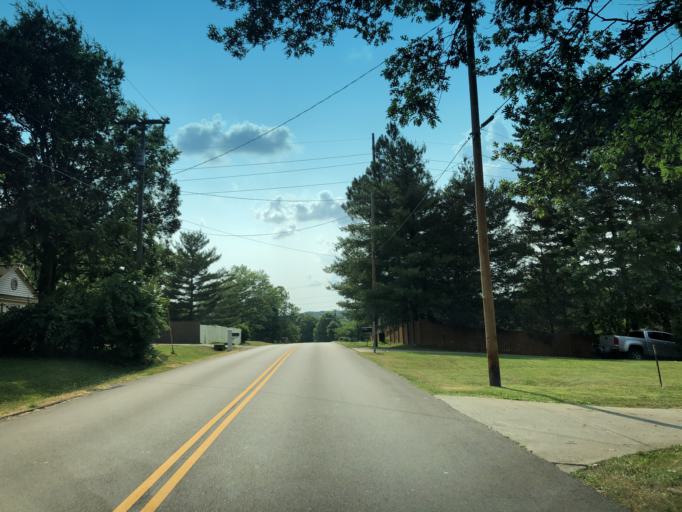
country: US
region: Tennessee
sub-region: Davidson County
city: Goodlettsville
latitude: 36.2736
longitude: -86.7202
